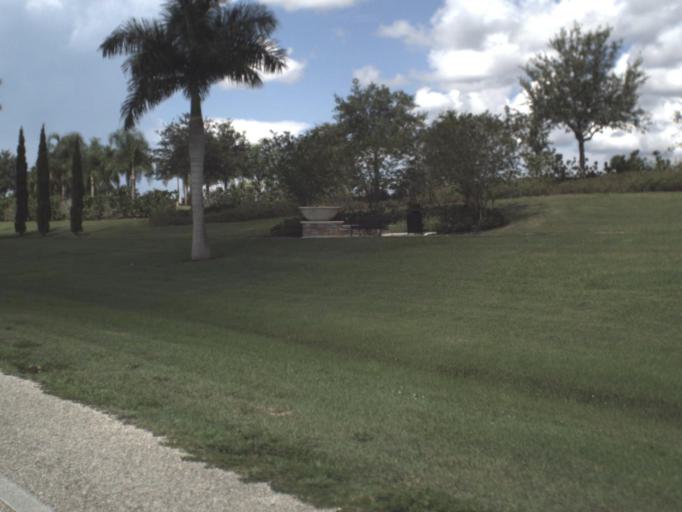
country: US
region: Florida
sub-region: Sarasota County
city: Plantation
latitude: 27.0497
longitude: -82.3385
